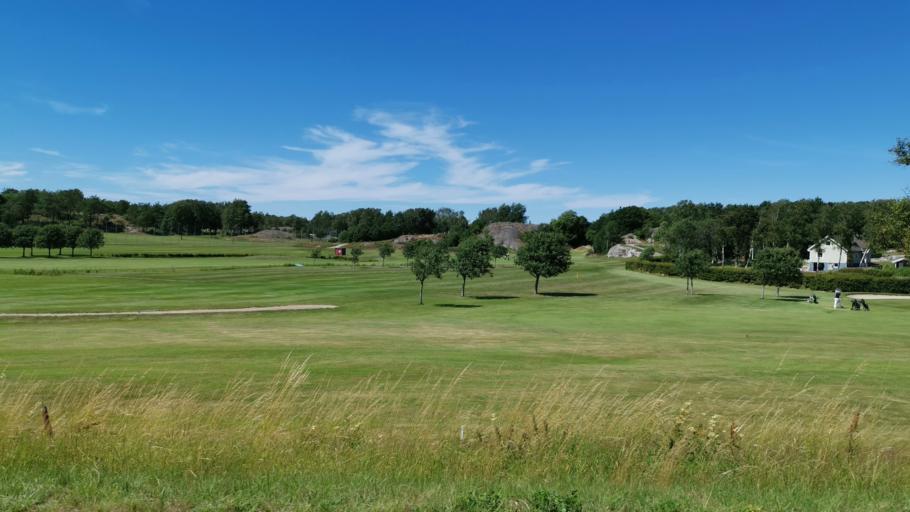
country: SE
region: Vaestra Goetaland
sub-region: Lysekils Kommun
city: Lysekil
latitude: 58.2335
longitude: 11.4555
